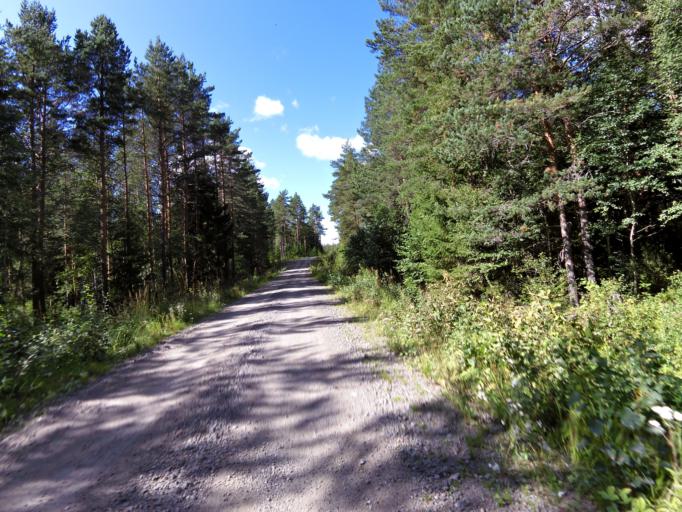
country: SE
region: Gaevleborg
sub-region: Ockelbo Kommun
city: Ockelbo
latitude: 60.7966
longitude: 16.8112
